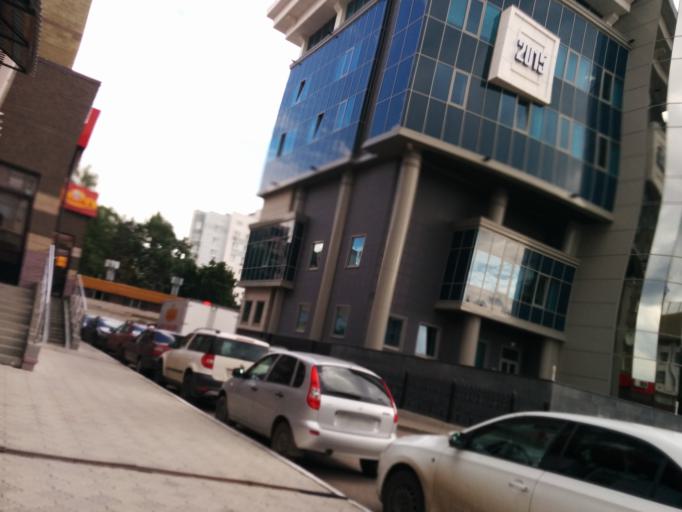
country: RU
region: Bashkortostan
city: Ufa
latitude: 54.7295
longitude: 55.9525
